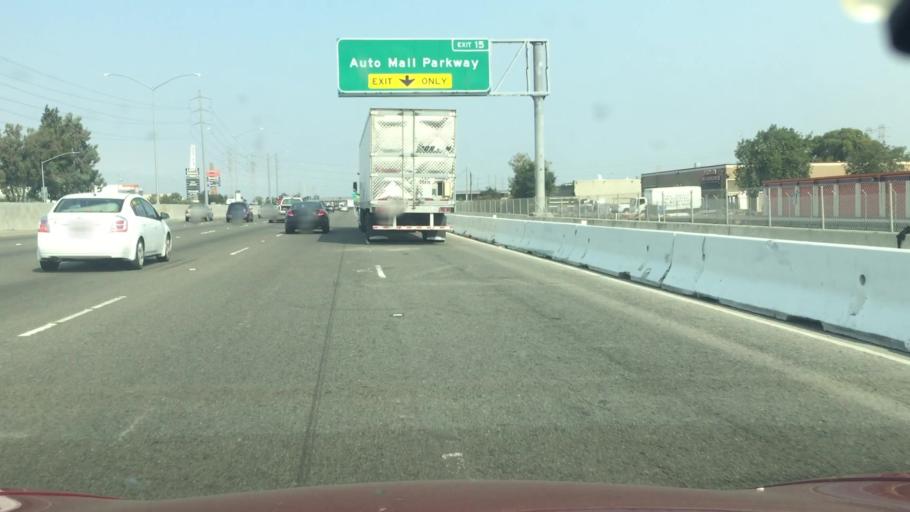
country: US
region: California
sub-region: Alameda County
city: Fremont
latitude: 37.5022
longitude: -121.9599
